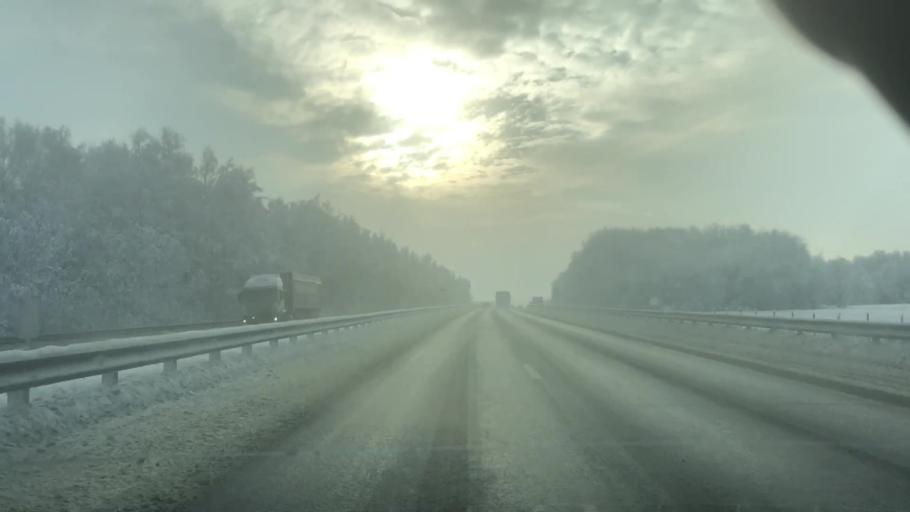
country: RU
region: Tula
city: Venev
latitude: 54.3825
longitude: 38.1550
